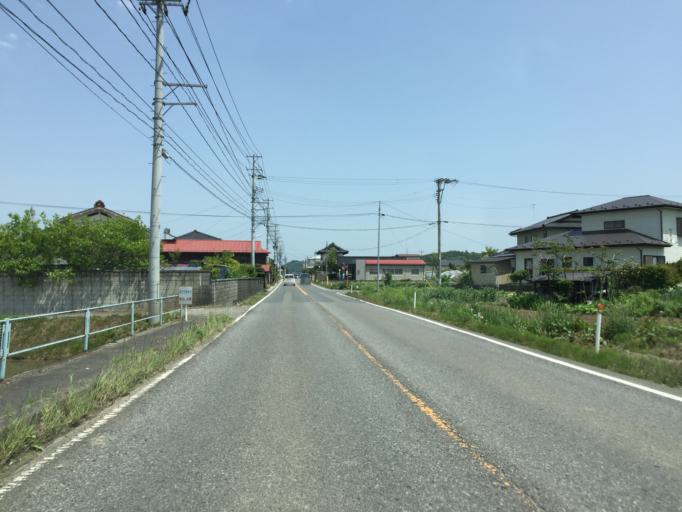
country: JP
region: Fukushima
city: Ishikawa
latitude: 37.1151
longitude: 140.2710
